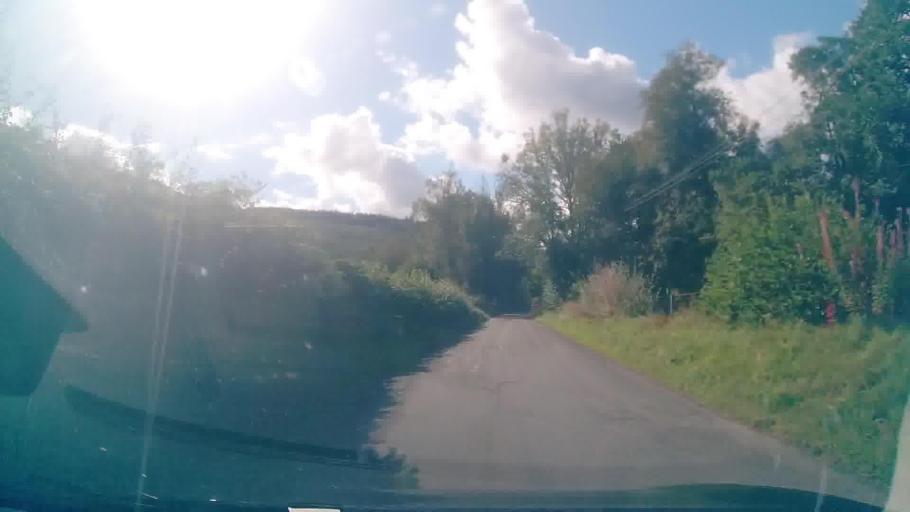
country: GB
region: Wales
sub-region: Sir Powys
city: Llangynog
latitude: 52.7695
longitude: -3.4185
